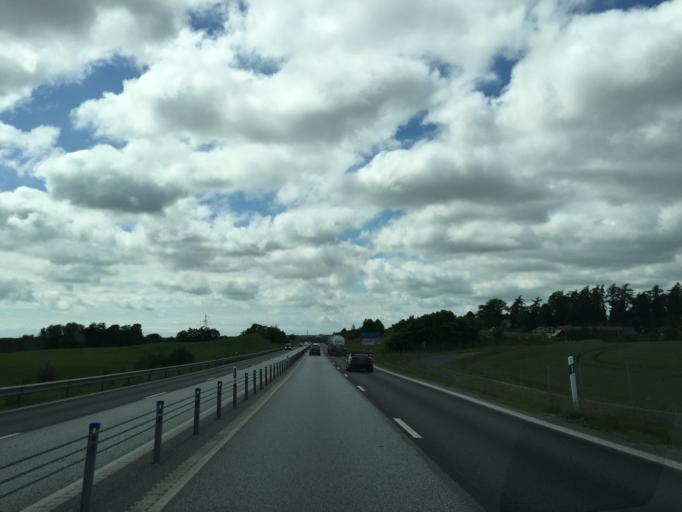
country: SE
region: Skane
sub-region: Trelleborgs Kommun
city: Anderslov
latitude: 55.5033
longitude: 13.3663
